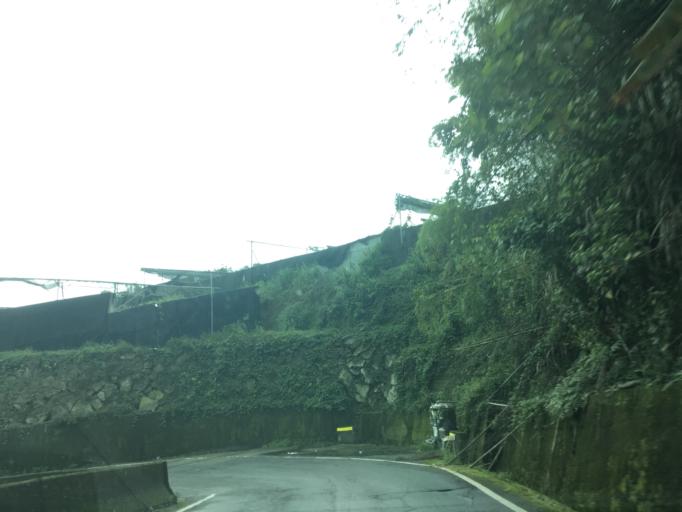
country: TW
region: Taiwan
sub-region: Chiayi
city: Jiayi Shi
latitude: 23.4476
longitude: 120.6674
